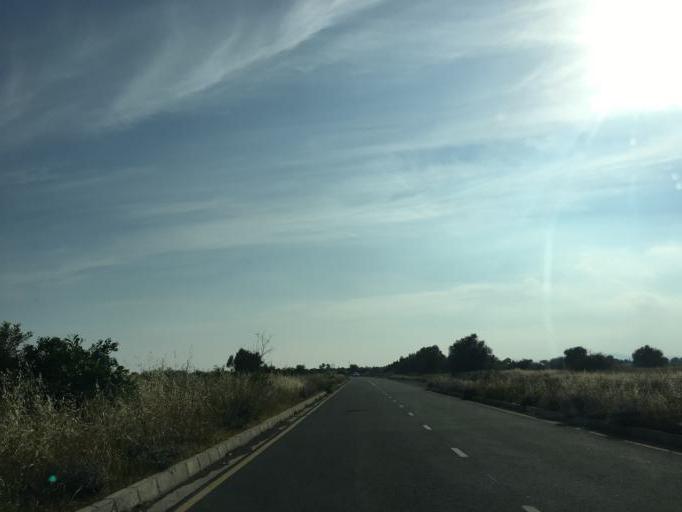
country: CY
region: Larnaka
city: Tersefanou
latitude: 34.8027
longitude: 33.5217
